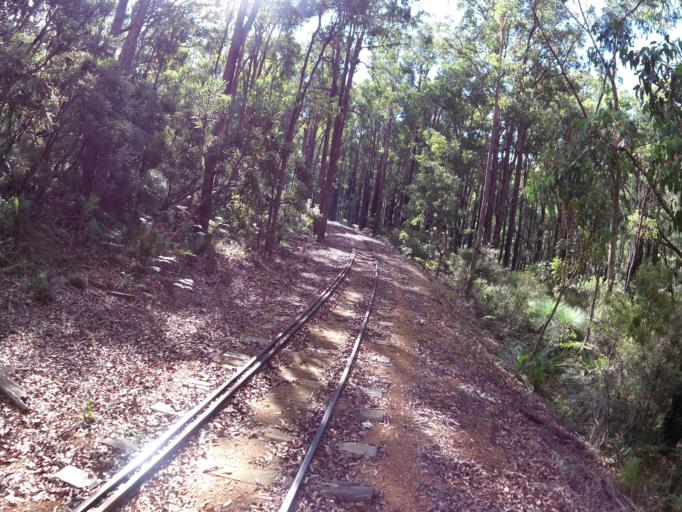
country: AU
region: Western Australia
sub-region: Waroona
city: Waroona
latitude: -32.7312
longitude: 116.1140
